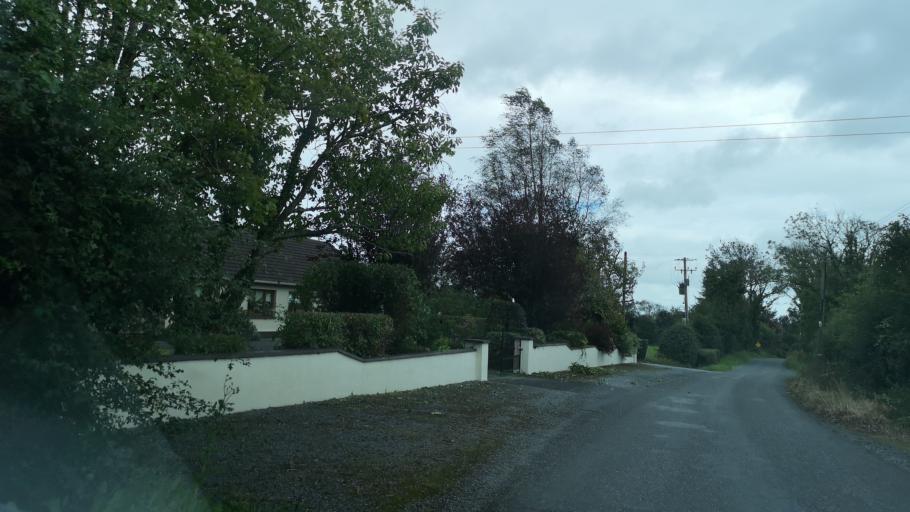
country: IE
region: Connaught
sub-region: County Galway
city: Loughrea
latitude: 53.3051
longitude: -8.6158
